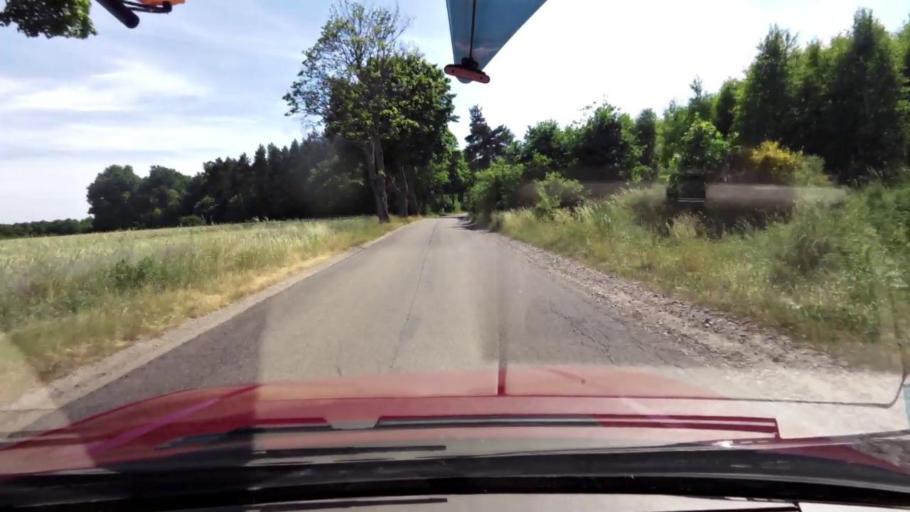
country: PL
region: Pomeranian Voivodeship
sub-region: Powiat slupski
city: Kobylnica
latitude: 54.3444
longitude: 16.9653
